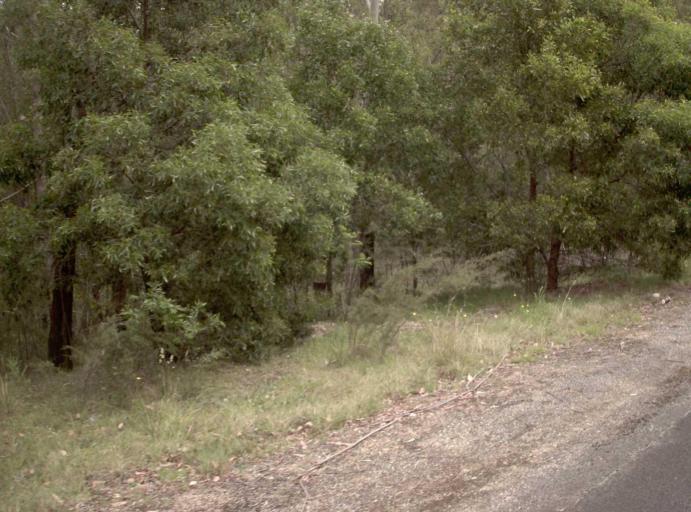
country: AU
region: New South Wales
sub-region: Bombala
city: Bombala
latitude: -37.2761
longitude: 149.2249
